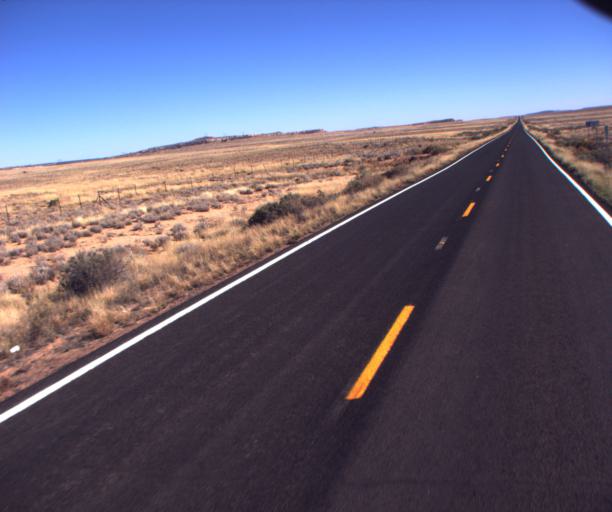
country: US
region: Arizona
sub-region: Navajo County
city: First Mesa
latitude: 35.9712
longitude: -110.7887
